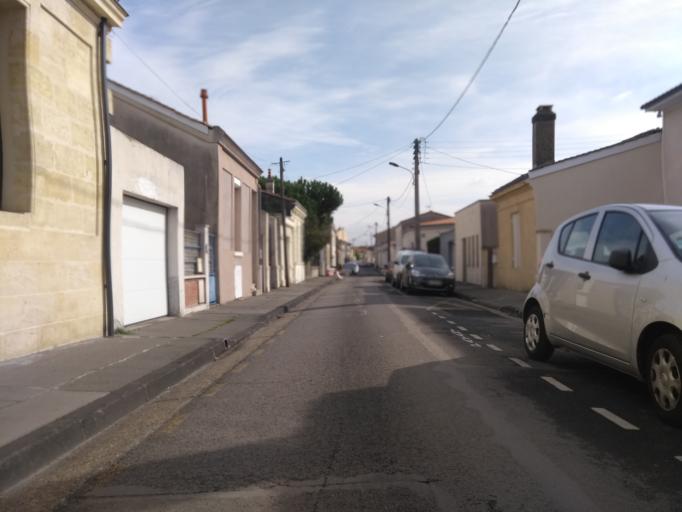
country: FR
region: Aquitaine
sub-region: Departement de la Gironde
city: Talence
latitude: 44.8227
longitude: -0.5968
